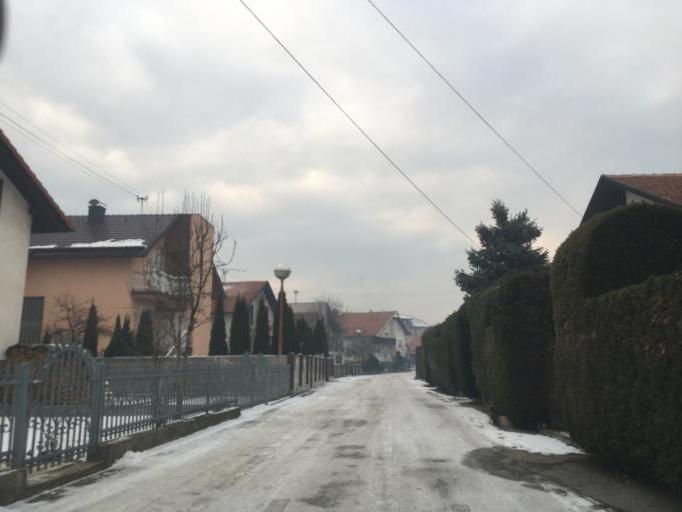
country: BA
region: Federation of Bosnia and Herzegovina
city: Bugojno
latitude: 44.0550
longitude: 17.4533
